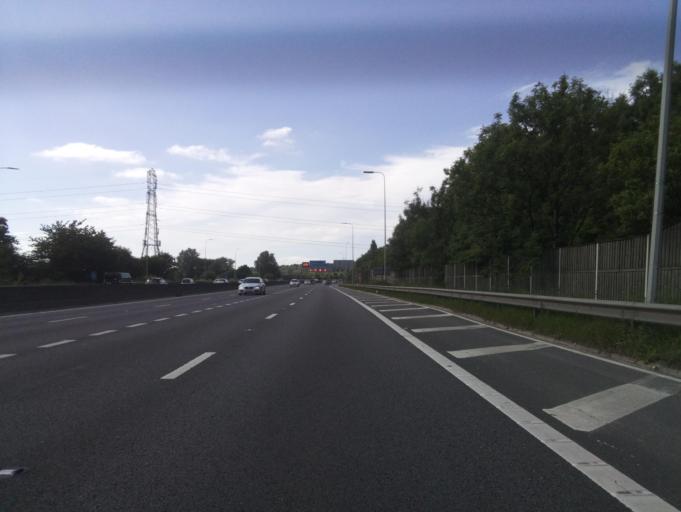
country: GB
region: England
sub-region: City and Borough of Salford
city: Walkden
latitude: 53.4924
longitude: -2.3806
